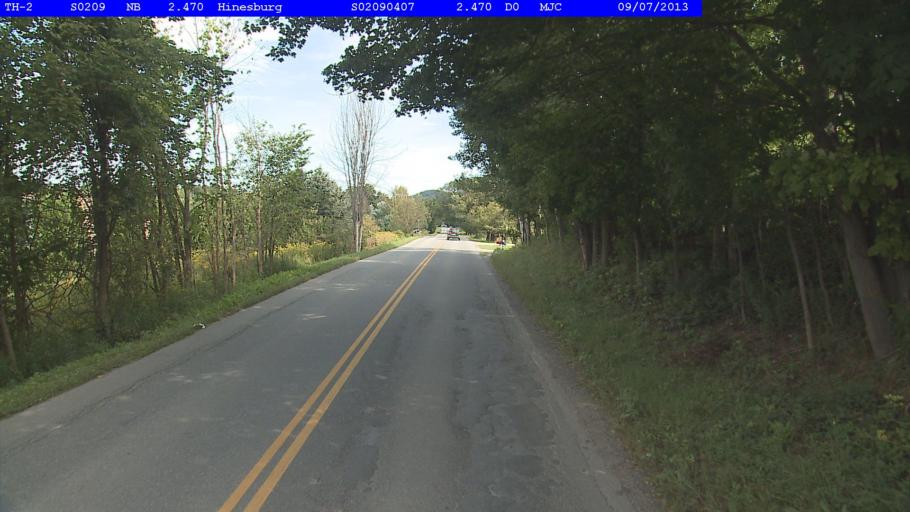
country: US
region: Vermont
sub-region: Chittenden County
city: Hinesburg
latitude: 44.3469
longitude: -73.0776
